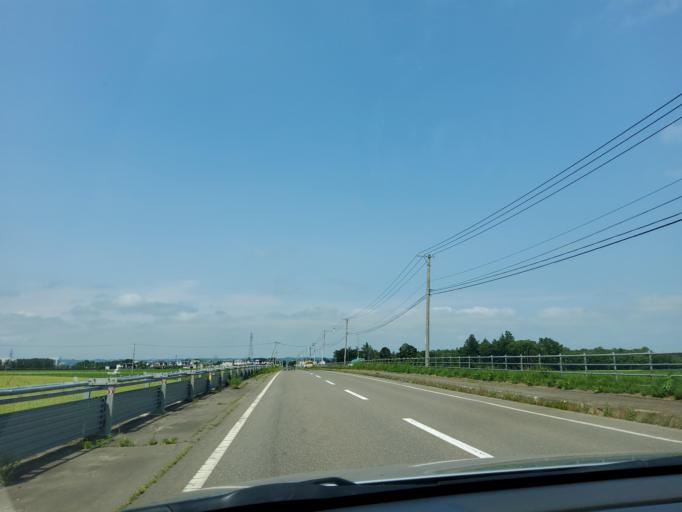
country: JP
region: Hokkaido
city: Obihiro
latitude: 42.8937
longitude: 143.0419
